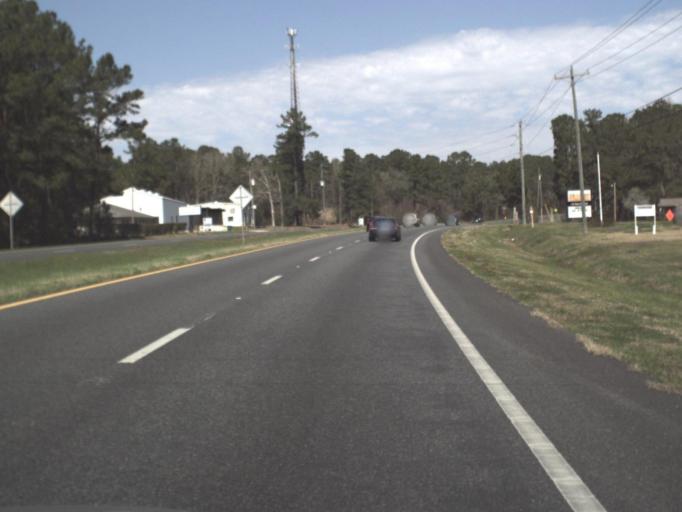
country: US
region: Florida
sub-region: Gadsden County
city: Havana
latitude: 30.6052
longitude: -84.4222
